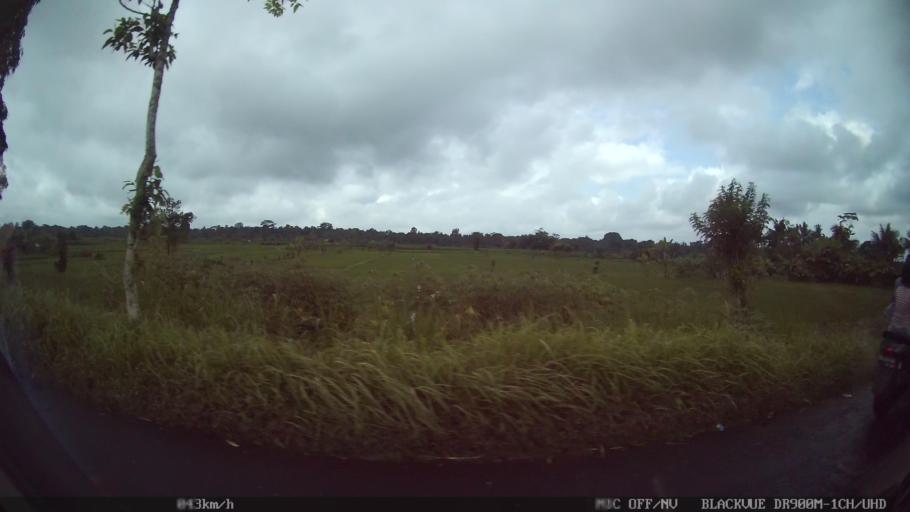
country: ID
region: Bali
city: Banjar Teguan
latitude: -8.5013
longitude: 115.2254
